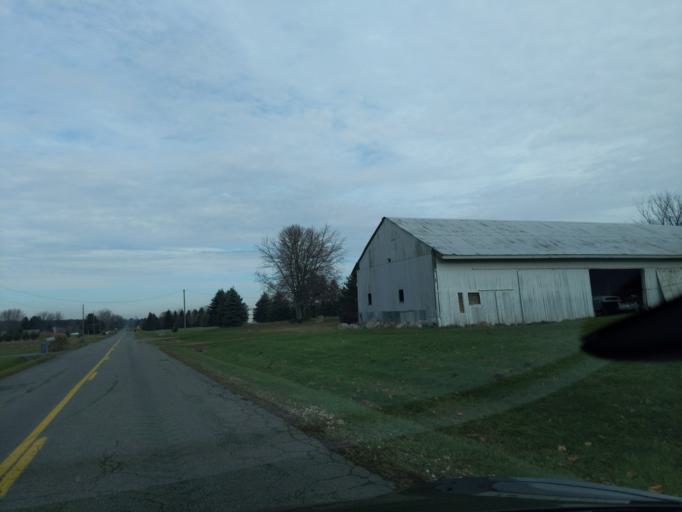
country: US
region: Michigan
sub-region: Ingham County
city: Leslie
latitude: 42.5058
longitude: -84.5024
